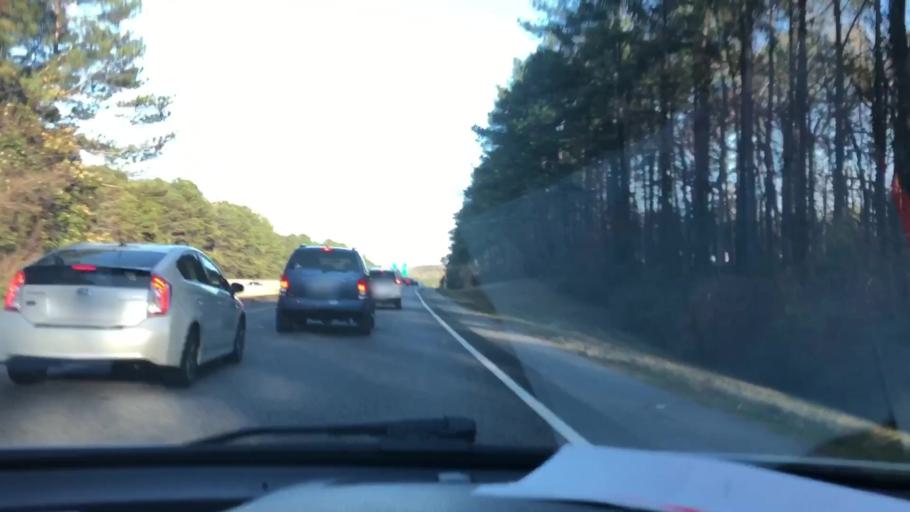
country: US
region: Georgia
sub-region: DeKalb County
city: Stone Mountain
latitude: 33.8199
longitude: -84.1678
